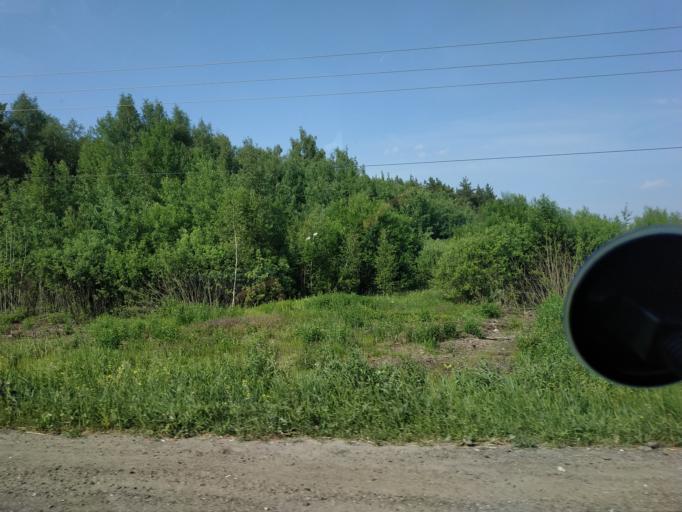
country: RU
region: Moskovskaya
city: Vostryakovo
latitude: 55.4076
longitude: 37.8603
